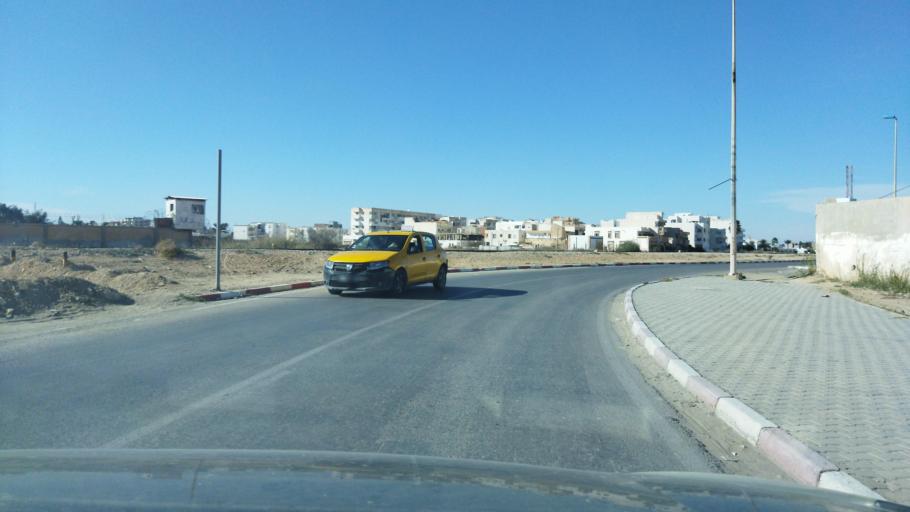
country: TN
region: Qabis
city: Gabes
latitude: 33.8874
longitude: 10.1166
